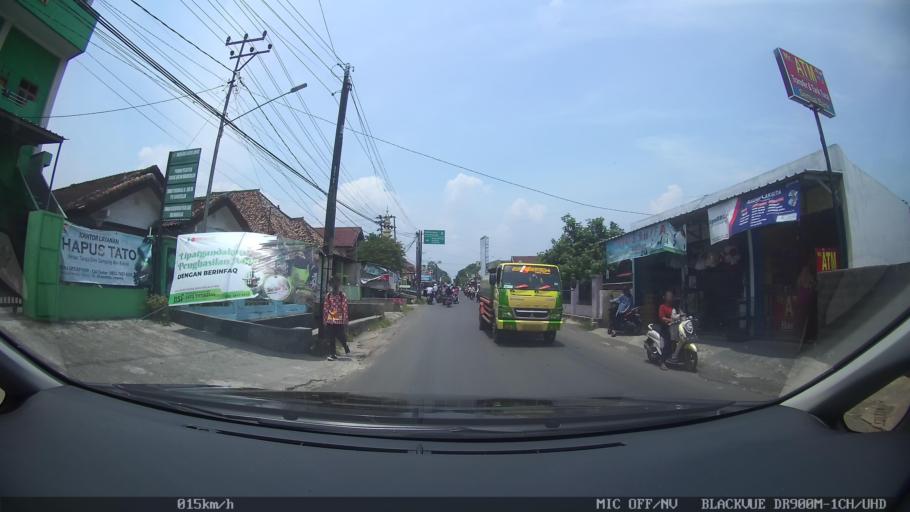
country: ID
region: Lampung
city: Bandarlampung
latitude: -5.4450
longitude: 105.2554
